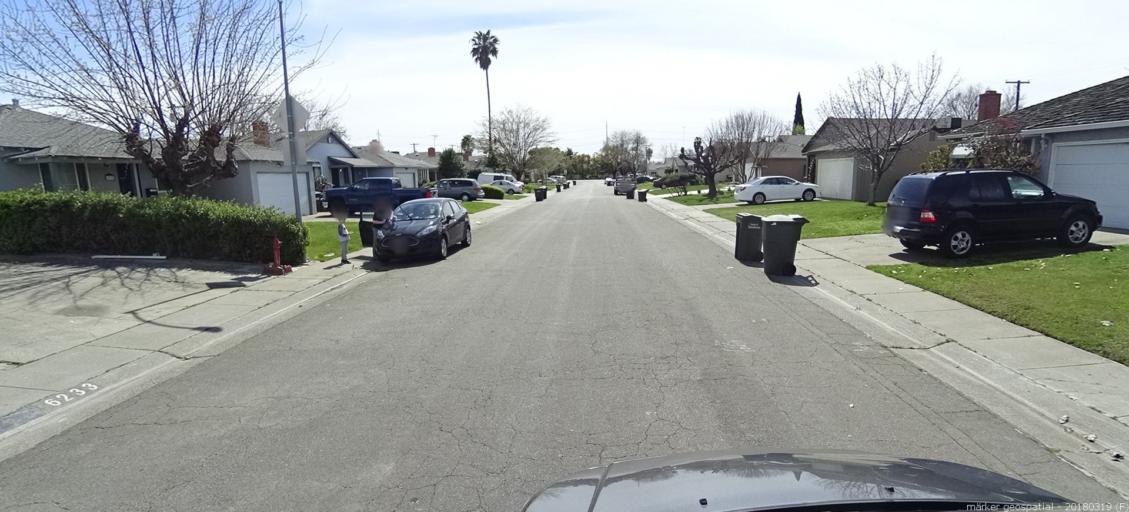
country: US
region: California
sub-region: Sacramento County
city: Parkway
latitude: 38.5120
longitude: -121.4536
